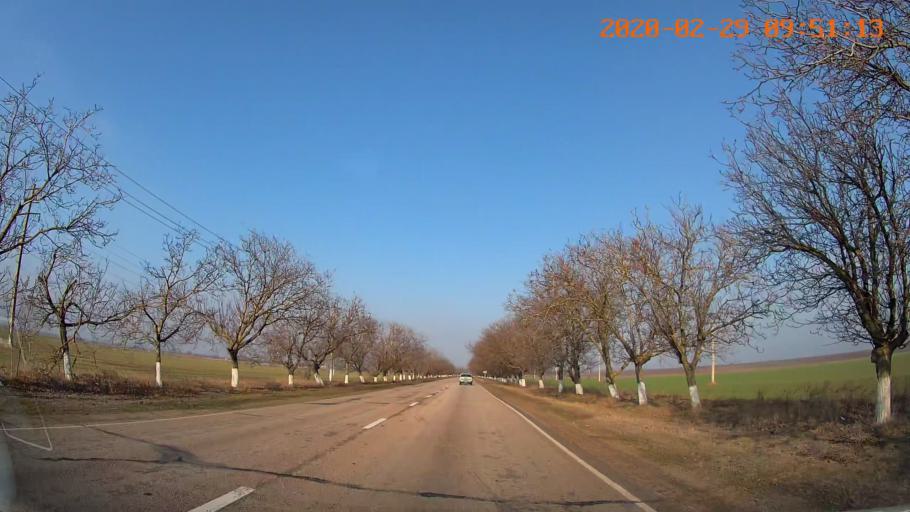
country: MD
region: Telenesti
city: Slobozia
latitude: 46.7068
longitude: 29.7430
